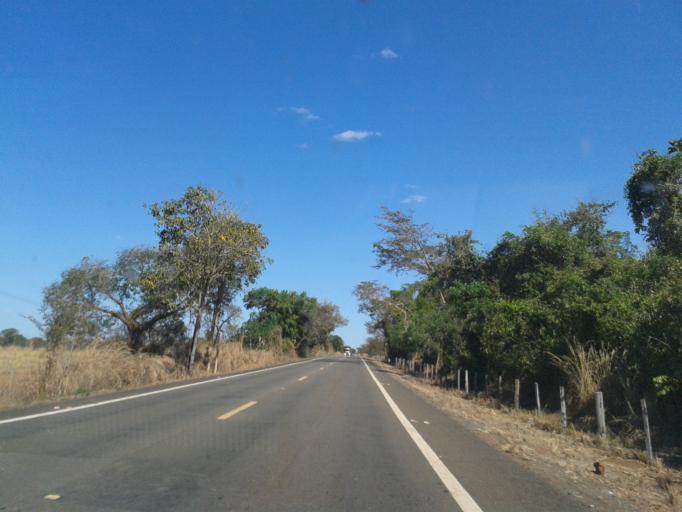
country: BR
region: Goias
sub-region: Sao Miguel Do Araguaia
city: Sao Miguel do Araguaia
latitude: -13.9036
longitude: -50.3260
